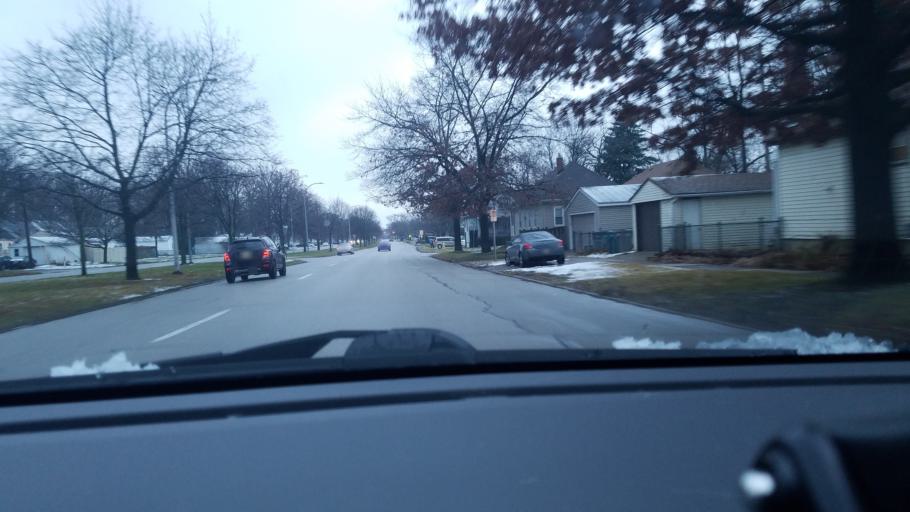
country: US
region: Michigan
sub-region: Wayne County
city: Dearborn Heights
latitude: 42.2942
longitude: -83.2539
